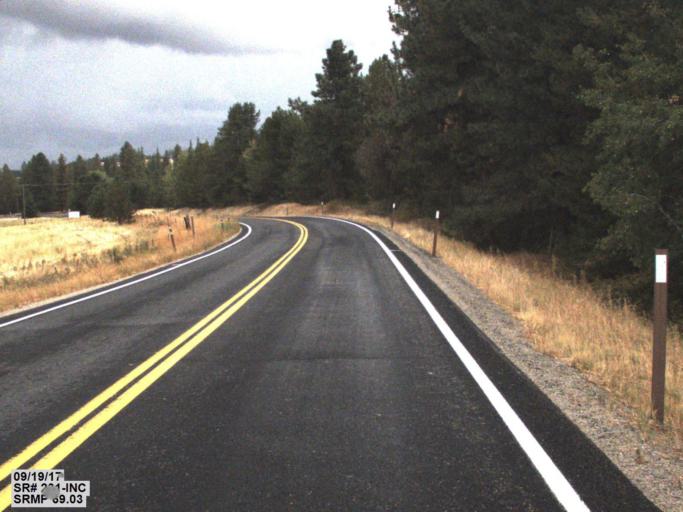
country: US
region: Washington
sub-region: Stevens County
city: Chewelah
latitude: 48.1375
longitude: -117.7338
